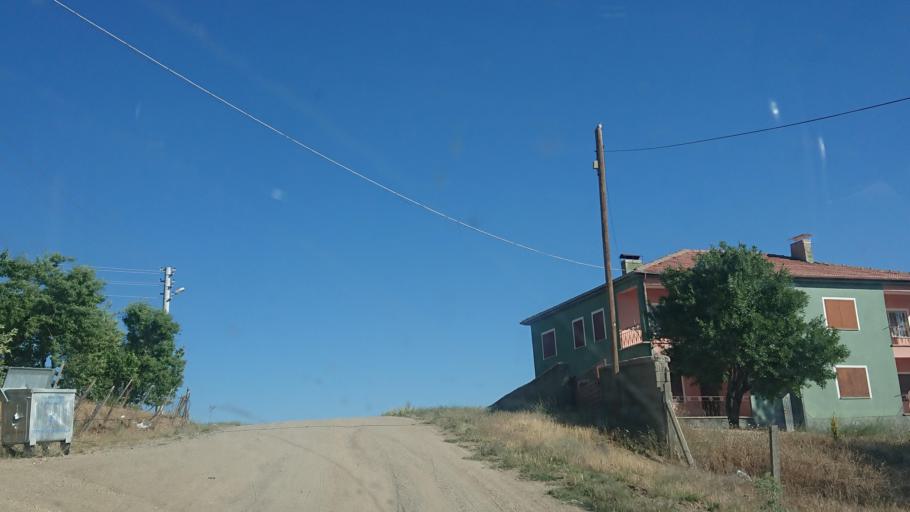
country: TR
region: Aksaray
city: Agacoren
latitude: 38.8736
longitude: 33.9428
